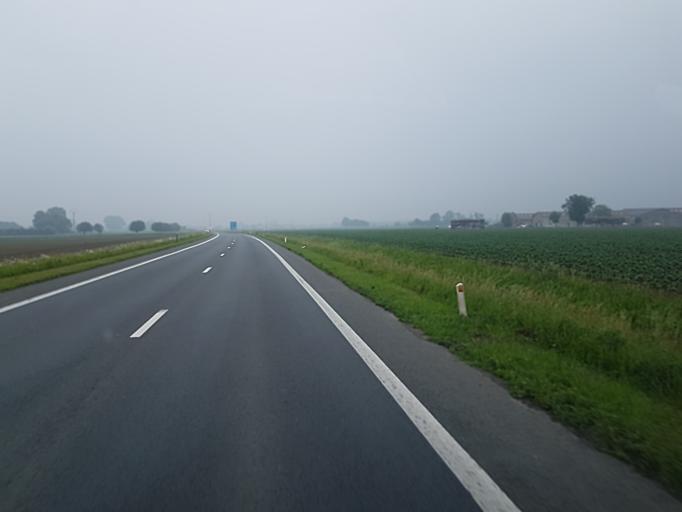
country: FR
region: Nord-Pas-de-Calais
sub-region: Departement du Nord
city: Bousbecque
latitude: 50.7987
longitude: 3.0781
